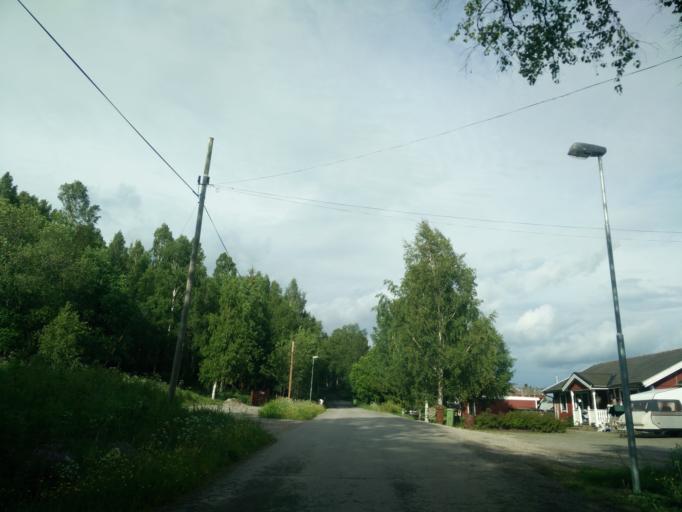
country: SE
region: Vaesternorrland
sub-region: Sundsvalls Kommun
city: Sundsvall
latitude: 62.4282
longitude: 17.2505
